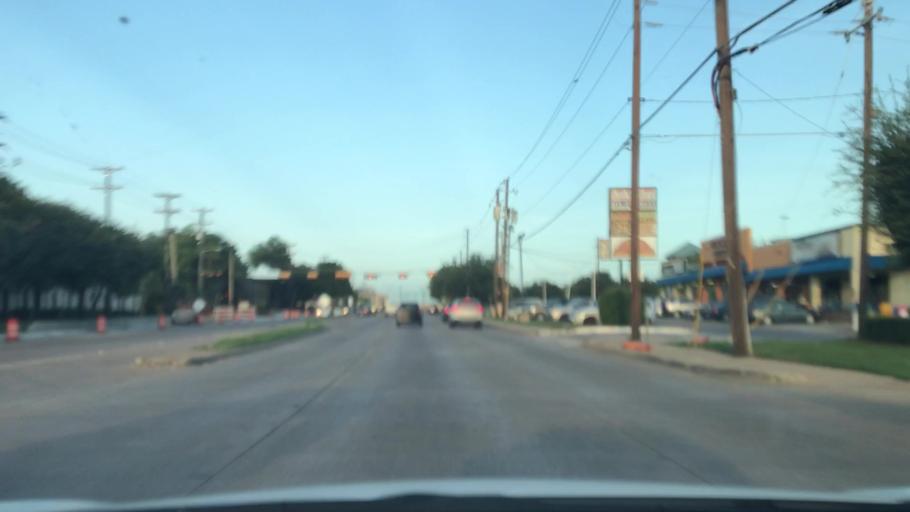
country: US
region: Texas
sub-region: Dallas County
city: Richardson
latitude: 32.9400
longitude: -96.7532
